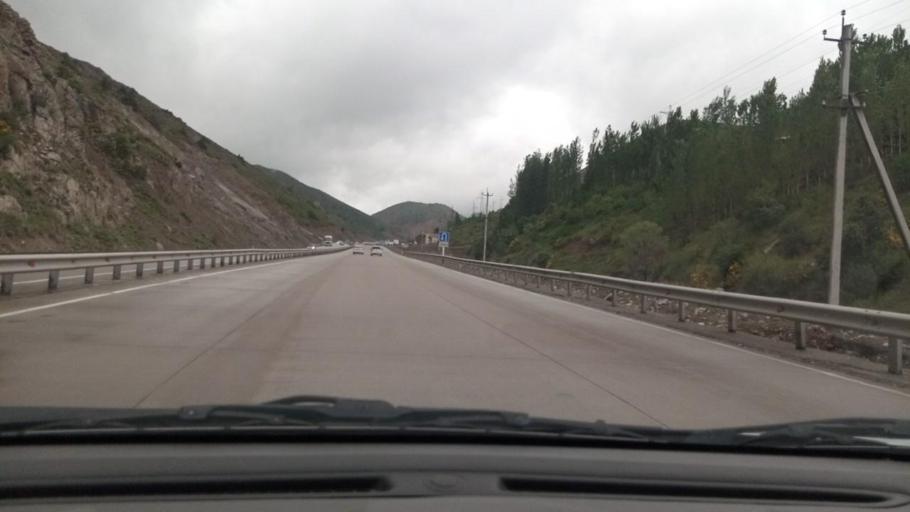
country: UZ
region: Toshkent
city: Angren
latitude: 41.0477
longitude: 70.5709
